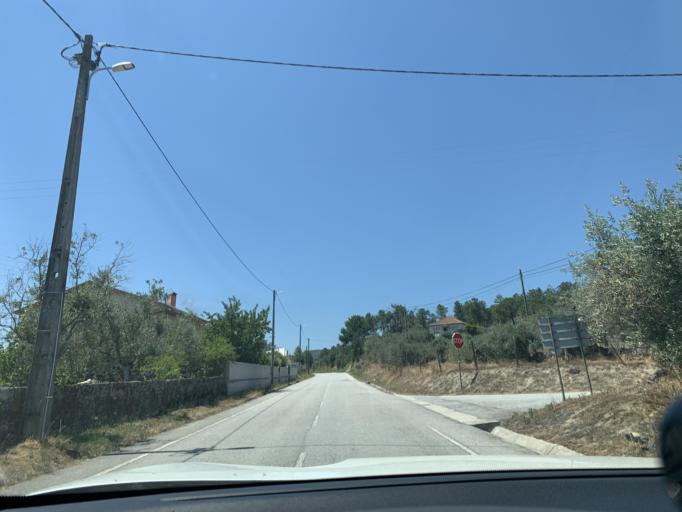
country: PT
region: Guarda
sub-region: Fornos de Algodres
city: Fornos de Algodres
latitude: 40.5793
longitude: -7.6118
